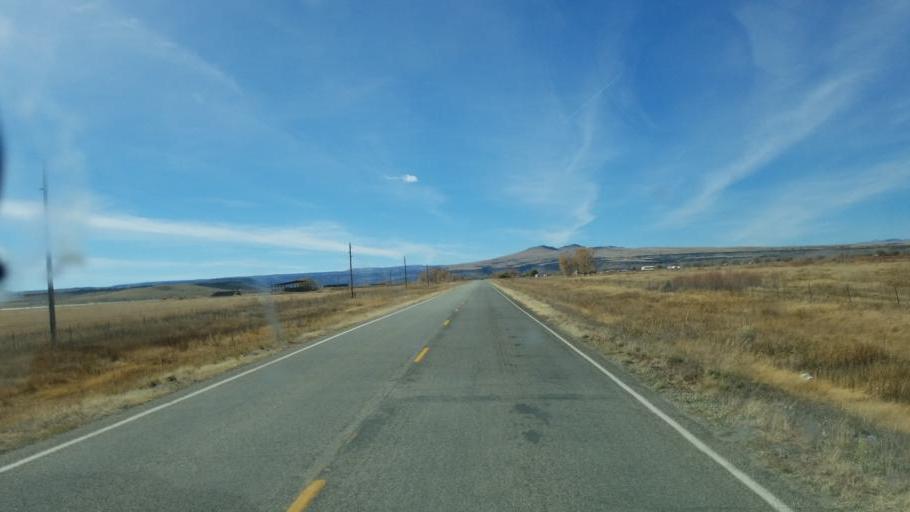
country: US
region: Colorado
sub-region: Conejos County
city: Conejos
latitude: 37.0646
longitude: -106.0410
